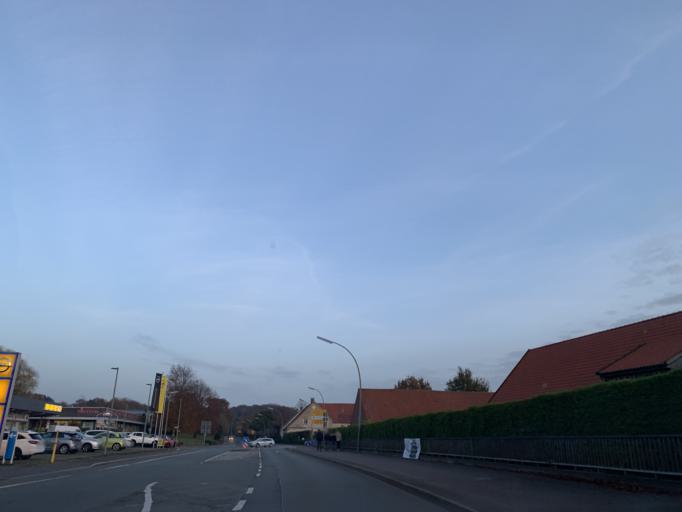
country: DE
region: North Rhine-Westphalia
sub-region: Regierungsbezirk Munster
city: Billerbeck
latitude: 51.9741
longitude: 7.2978
